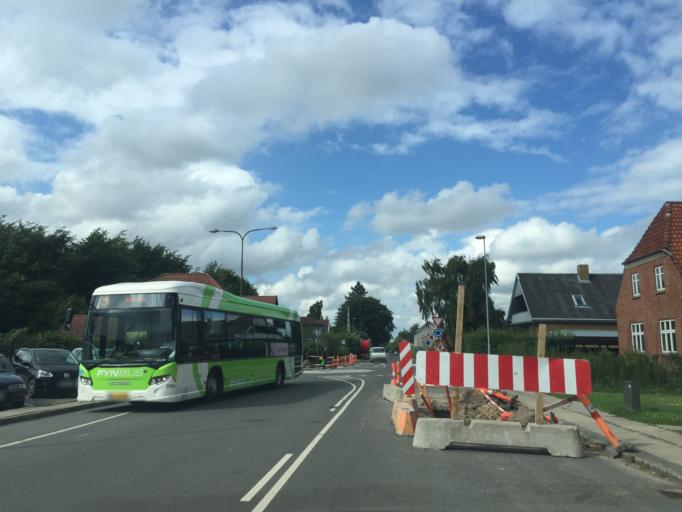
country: DK
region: South Denmark
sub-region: Odense Kommune
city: Odense
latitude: 55.3588
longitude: 10.3900
